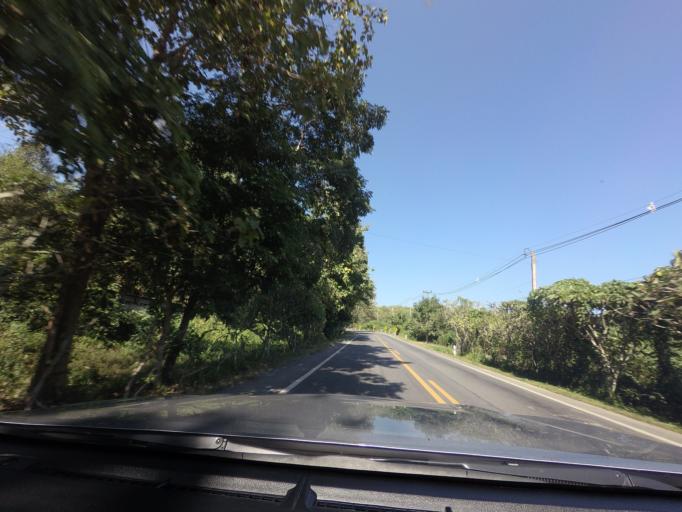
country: TH
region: Sukhothai
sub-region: Amphoe Si Satchanalai
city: Si Satchanalai
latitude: 17.6138
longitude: 99.7086
